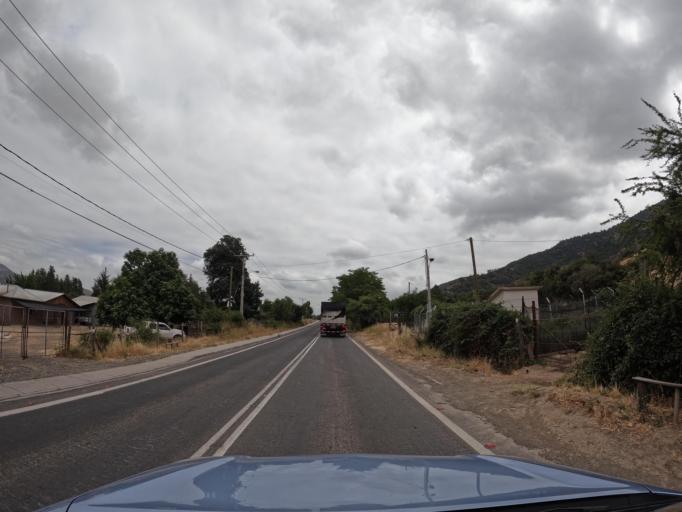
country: CL
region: Maule
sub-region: Provincia de Curico
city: Teno
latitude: -34.7992
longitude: -71.2246
